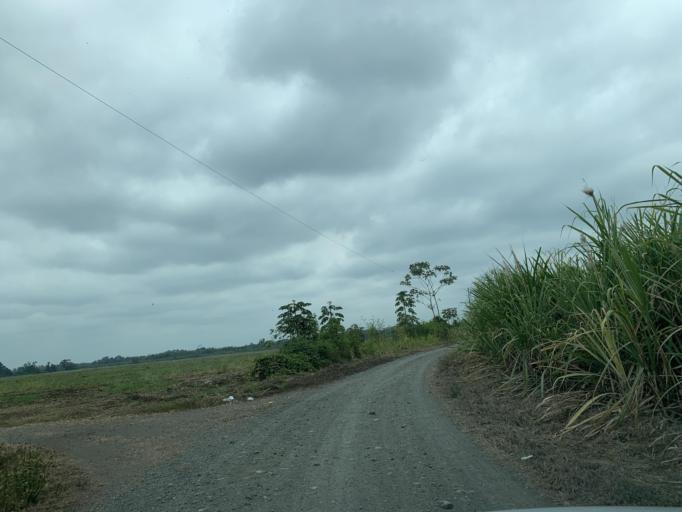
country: EC
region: Canar
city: La Troncal
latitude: -2.3509
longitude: -79.4608
